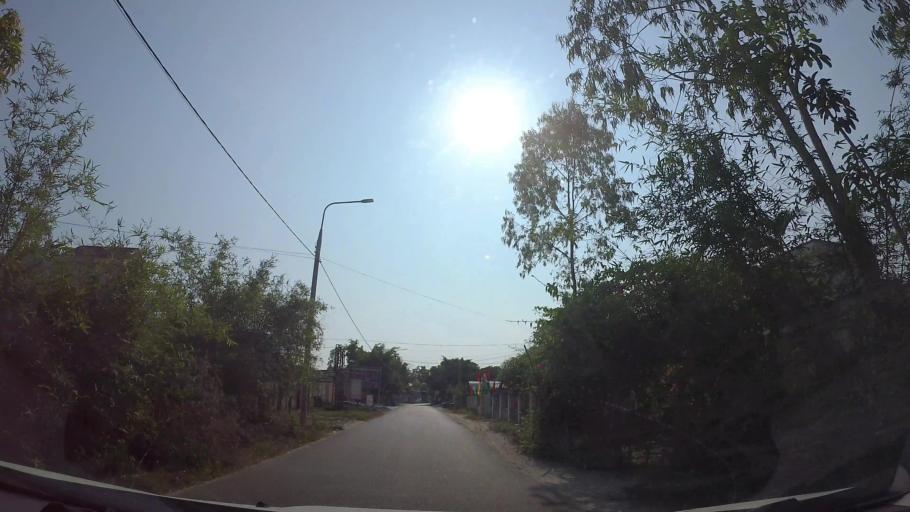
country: VN
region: Quang Nam
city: Quang Nam
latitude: 15.9491
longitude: 108.2686
